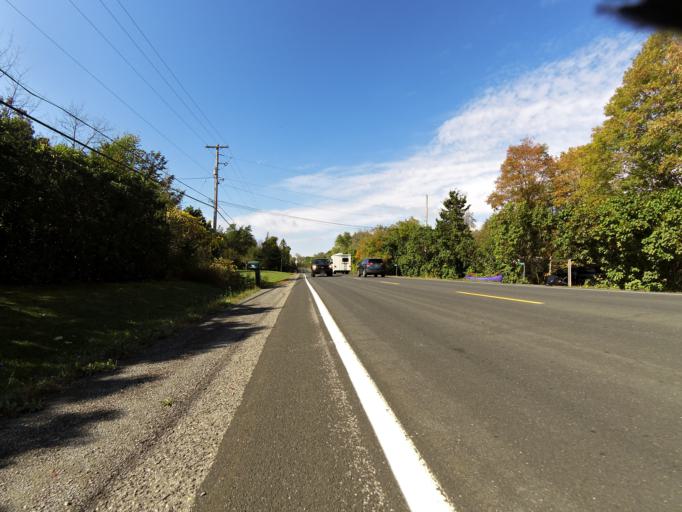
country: CA
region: Ontario
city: Picton
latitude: 44.0443
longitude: -77.0829
